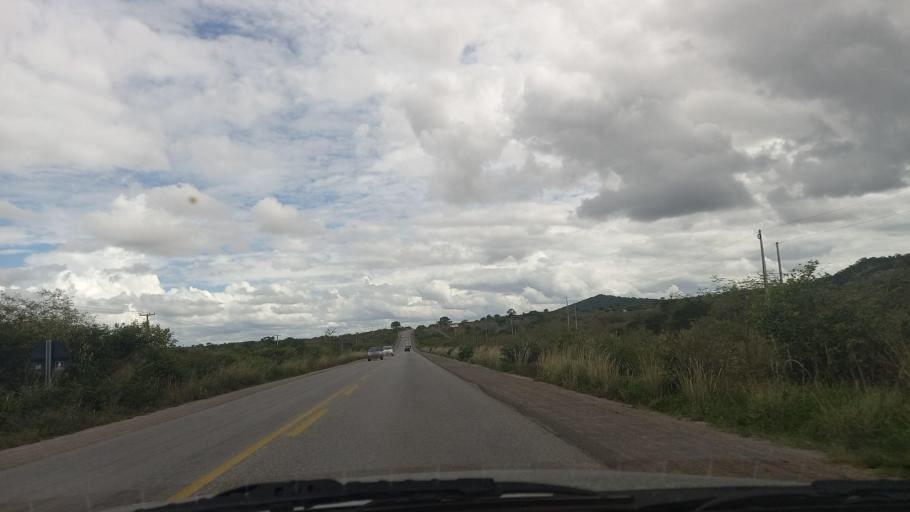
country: BR
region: Pernambuco
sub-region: Cachoeirinha
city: Cachoeirinha
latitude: -8.3395
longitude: -36.1593
